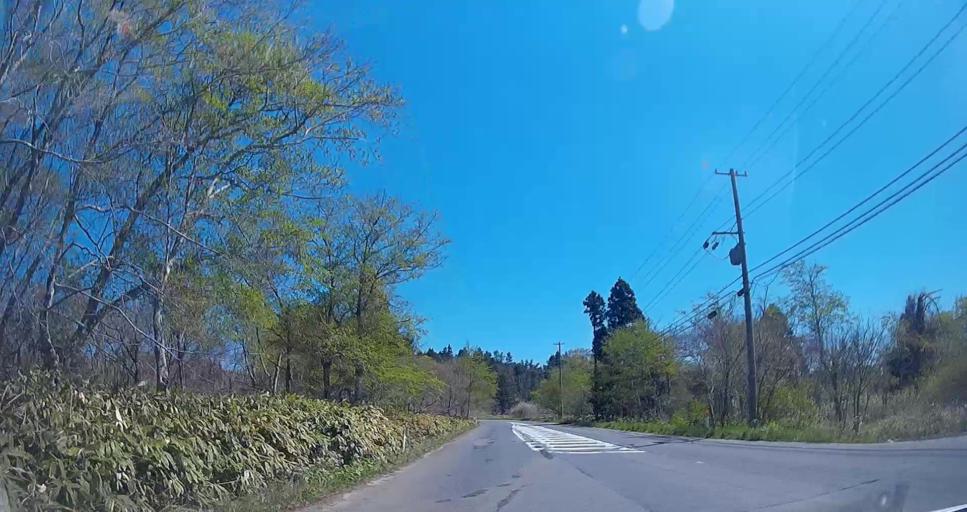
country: JP
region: Aomori
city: Misawa
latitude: 40.9081
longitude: 141.3731
